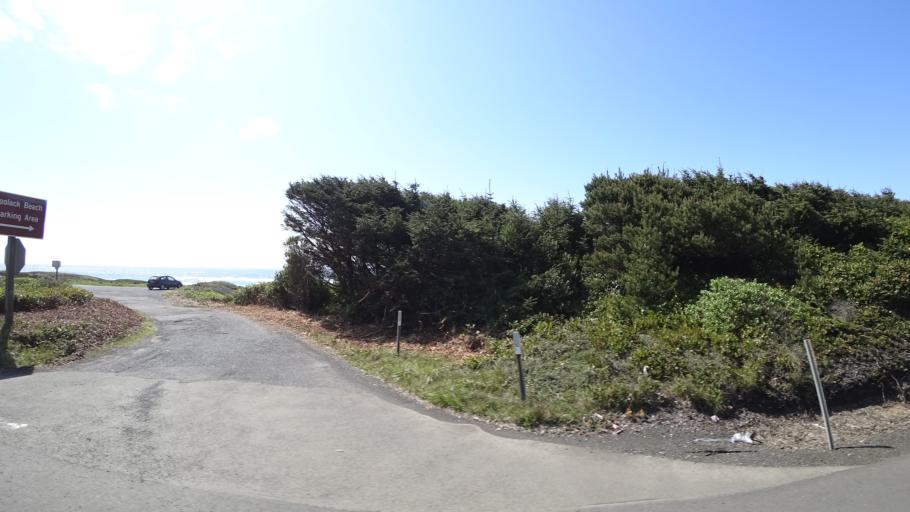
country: US
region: Oregon
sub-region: Lincoln County
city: Newport
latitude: 44.7047
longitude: -124.0608
